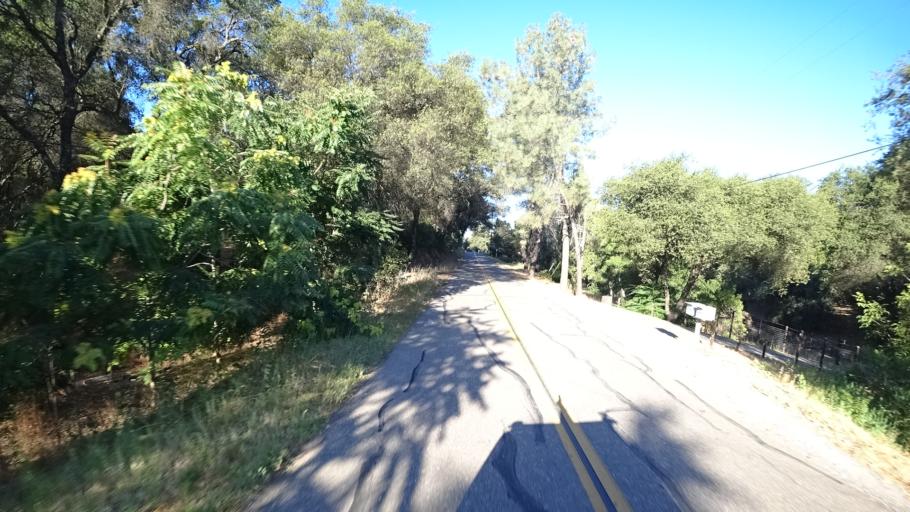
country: US
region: California
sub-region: Amador County
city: Jackson
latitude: 38.3019
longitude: -120.7130
